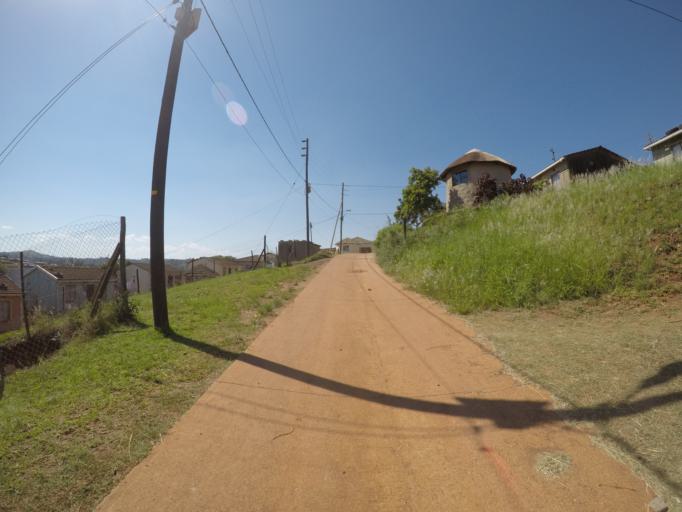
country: ZA
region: KwaZulu-Natal
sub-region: uThungulu District Municipality
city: Empangeni
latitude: -28.7701
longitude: 31.8759
